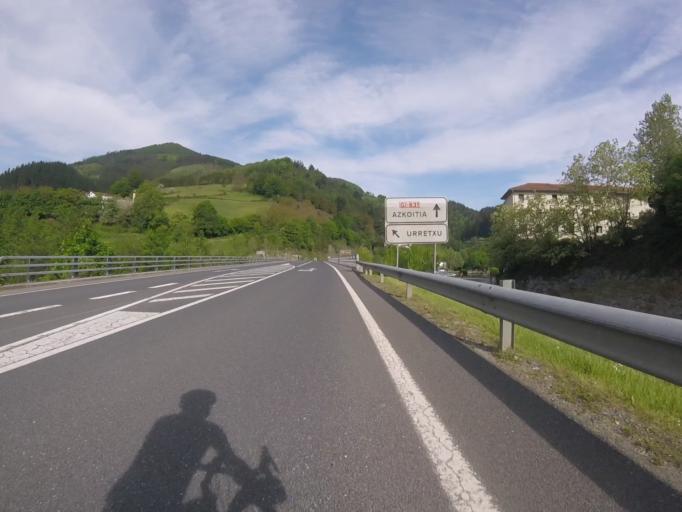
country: ES
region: Basque Country
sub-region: Provincia de Guipuzcoa
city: Urretxu
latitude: 43.0983
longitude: -2.3162
